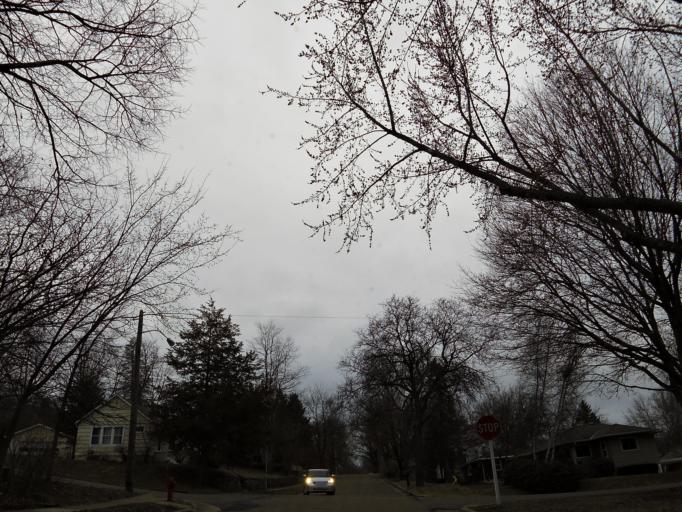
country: US
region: Wisconsin
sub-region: Saint Croix County
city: Hudson
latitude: 44.9807
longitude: -92.7452
